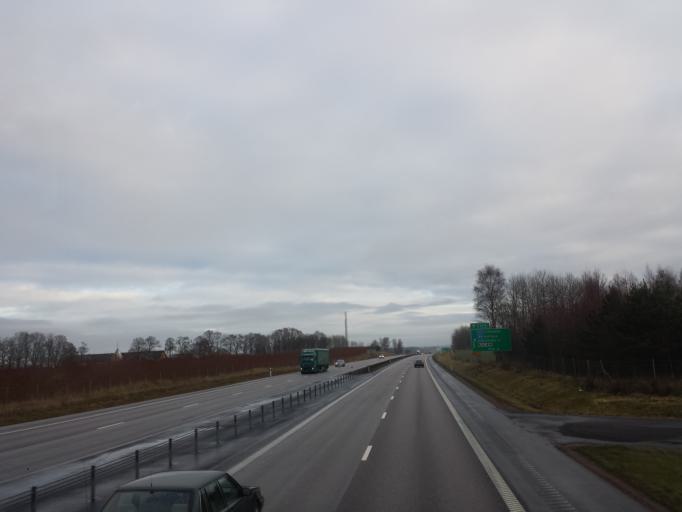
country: SE
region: OEstergoetland
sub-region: Linkopings Kommun
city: Malmslatt
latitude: 58.4298
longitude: 15.5103
